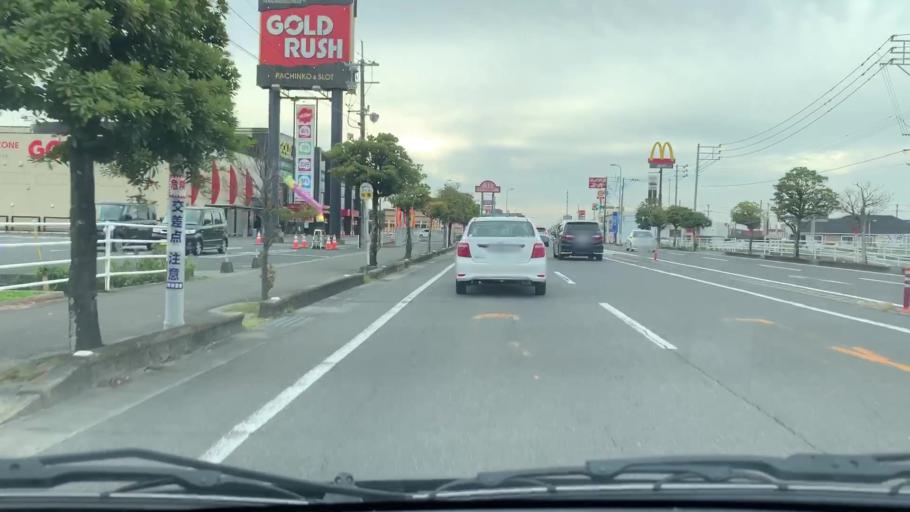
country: JP
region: Saga Prefecture
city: Saga-shi
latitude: 33.2940
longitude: 130.2844
